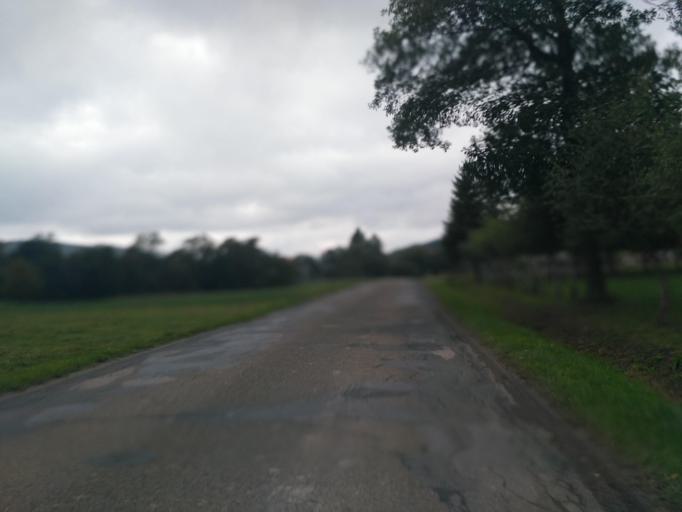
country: PL
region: Subcarpathian Voivodeship
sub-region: Powiat debicki
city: Brzostek
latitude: 49.9200
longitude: 21.4457
